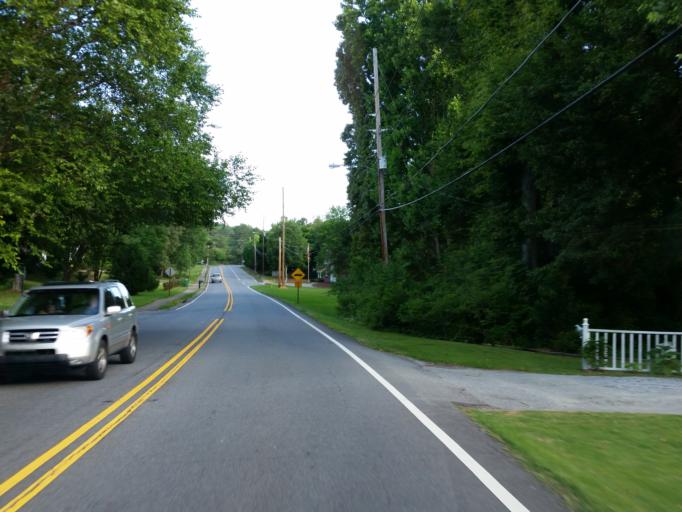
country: US
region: Georgia
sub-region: Cherokee County
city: Woodstock
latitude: 34.0601
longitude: -84.4864
